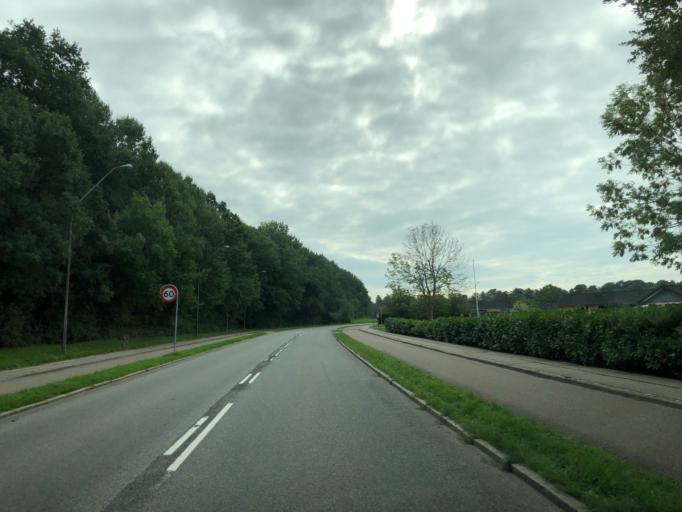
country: DK
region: South Denmark
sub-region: Sonderborg Kommune
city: Sonderborg
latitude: 54.9016
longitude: 9.8243
